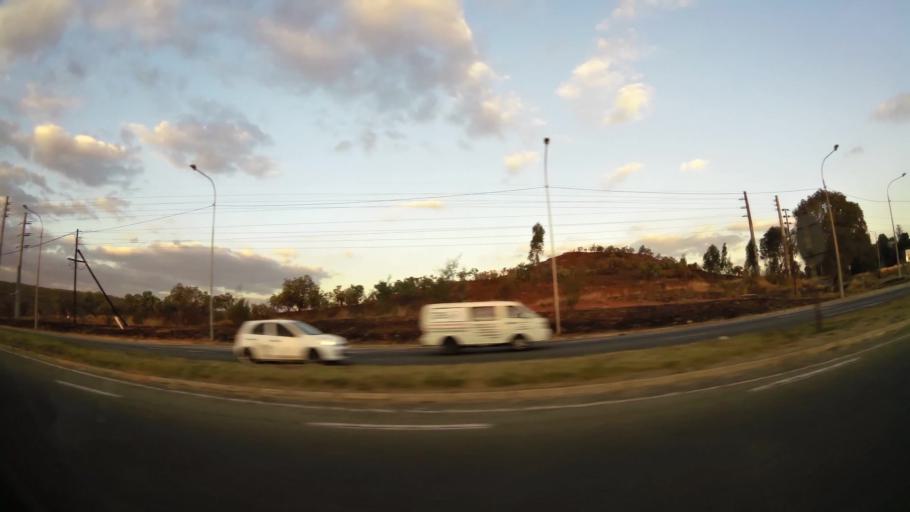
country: ZA
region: Gauteng
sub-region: West Rand District Municipality
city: Krugersdorp
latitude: -26.0712
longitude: 27.8015
